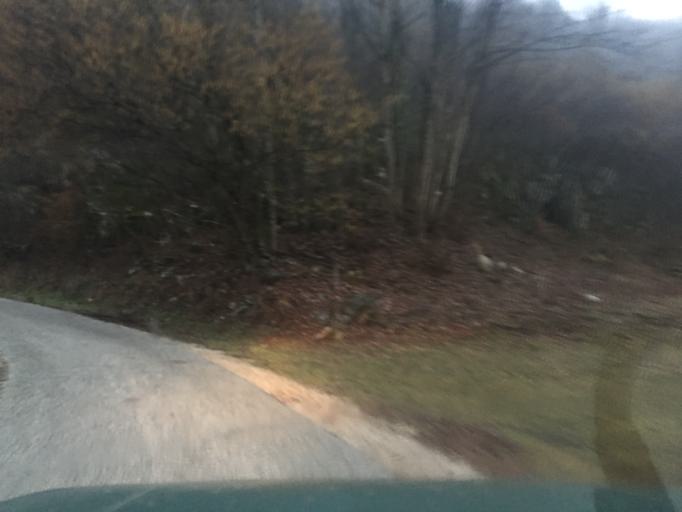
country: SI
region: Kanal
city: Kanal
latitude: 46.0534
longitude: 13.6669
